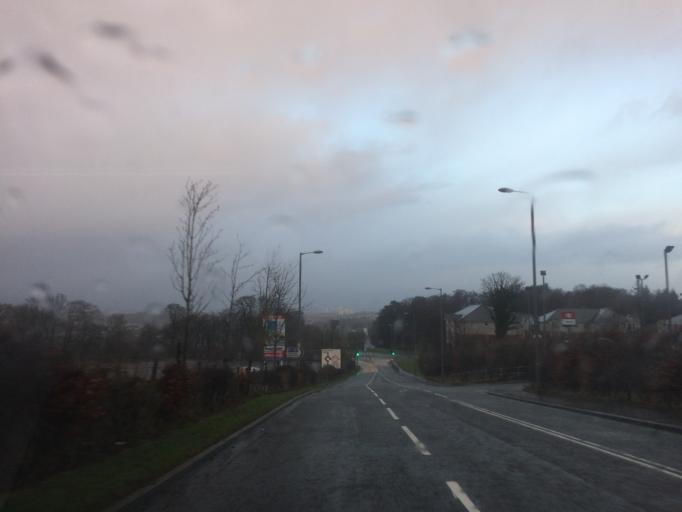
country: GB
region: Scotland
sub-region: East Renfrewshire
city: Newton Mearns
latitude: 55.7906
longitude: -4.3367
